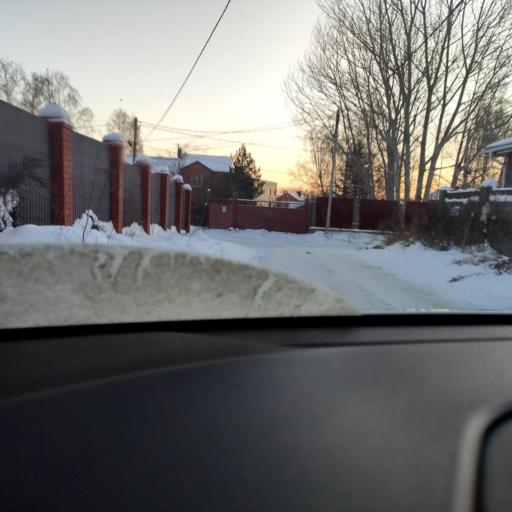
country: RU
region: Tatarstan
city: Stolbishchi
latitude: 55.7482
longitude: 49.2524
